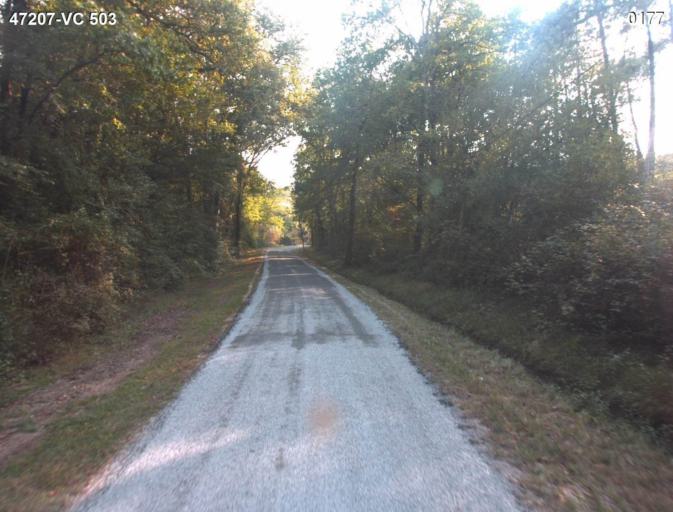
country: FR
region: Aquitaine
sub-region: Departement du Lot-et-Garonne
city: Barbaste
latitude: 44.2047
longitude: 0.2340
